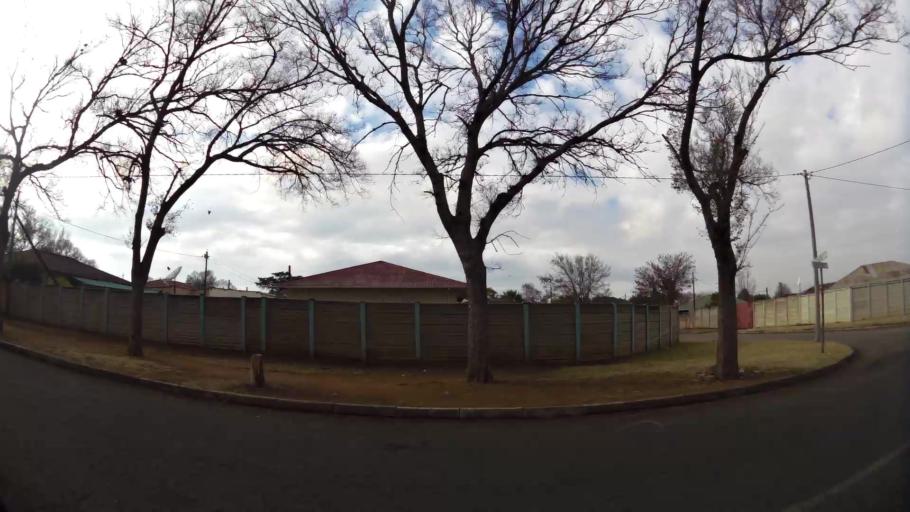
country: ZA
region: Gauteng
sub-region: Sedibeng District Municipality
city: Vanderbijlpark
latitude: -26.6938
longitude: 27.8146
